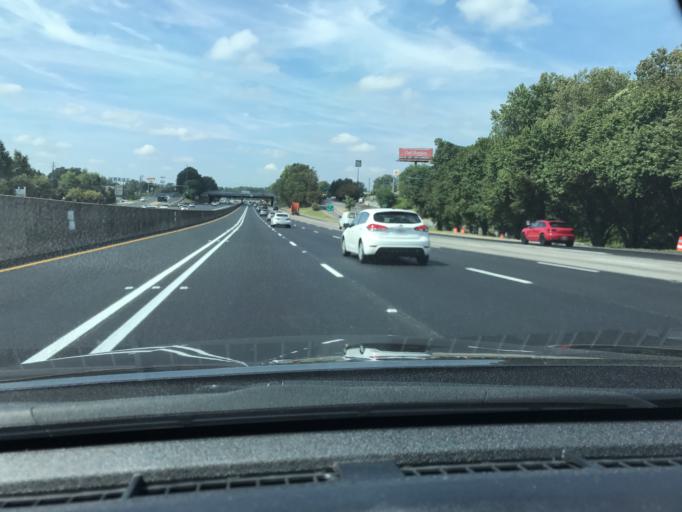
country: US
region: Georgia
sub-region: DeKalb County
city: Chamblee
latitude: 33.8682
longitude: -84.2848
